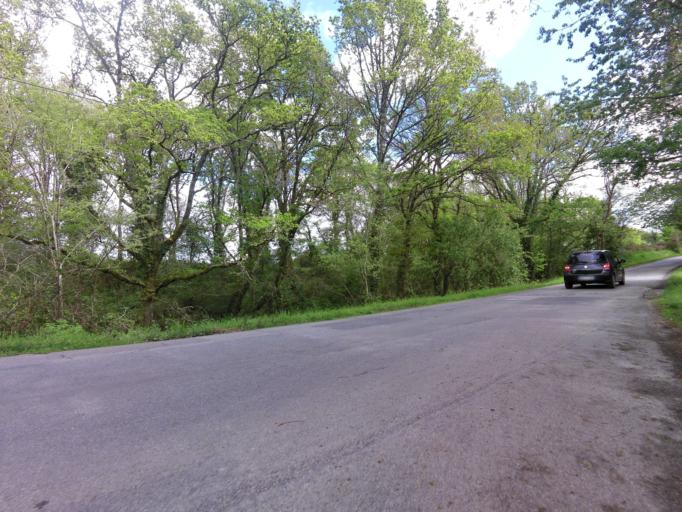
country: FR
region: Brittany
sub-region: Departement du Morbihan
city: Plougoumelen
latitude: 47.6452
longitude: -2.9233
